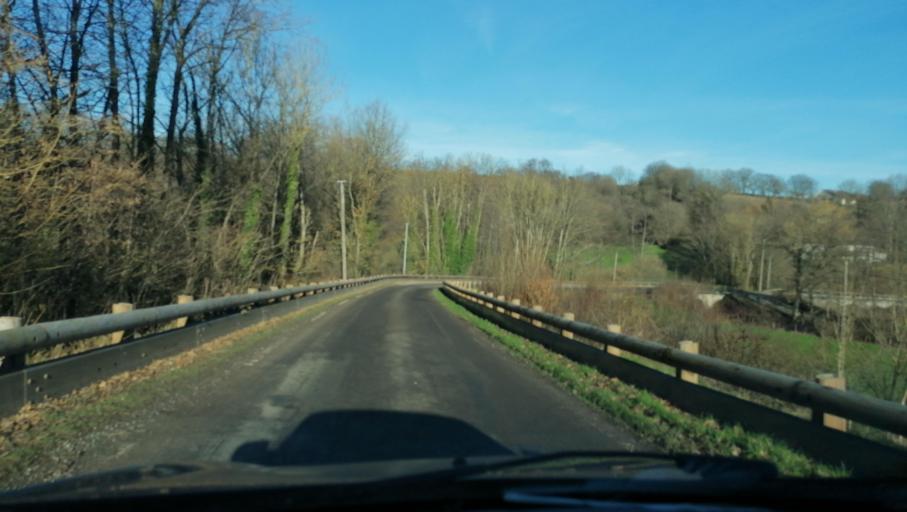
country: FR
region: Nord-Pas-de-Calais
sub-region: Departement du Nord
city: Recquignies
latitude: 50.2045
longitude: 4.0655
